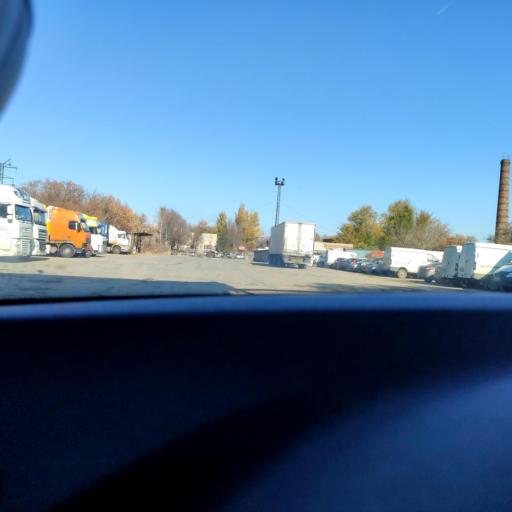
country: RU
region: Samara
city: Petra-Dubrava
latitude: 53.2575
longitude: 50.2981
